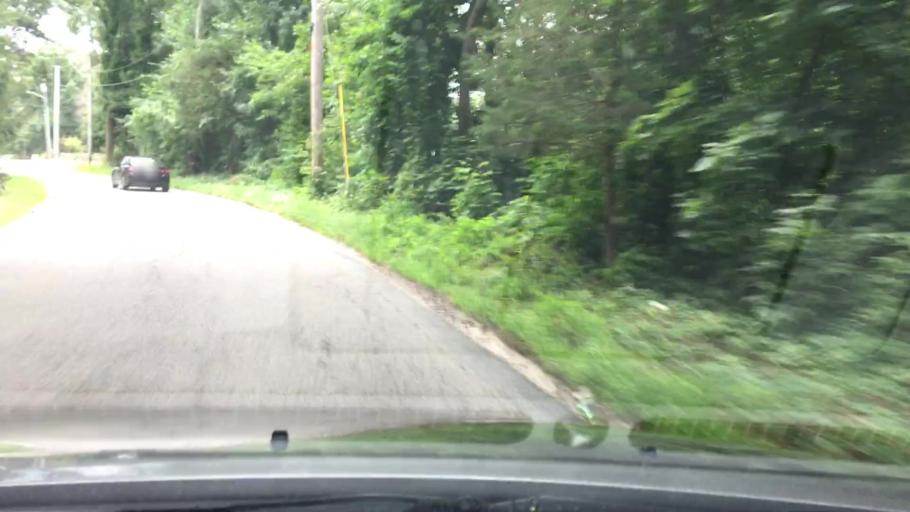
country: US
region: Rhode Island
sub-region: Providence County
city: Cumberland Hill
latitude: 42.0174
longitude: -71.4502
